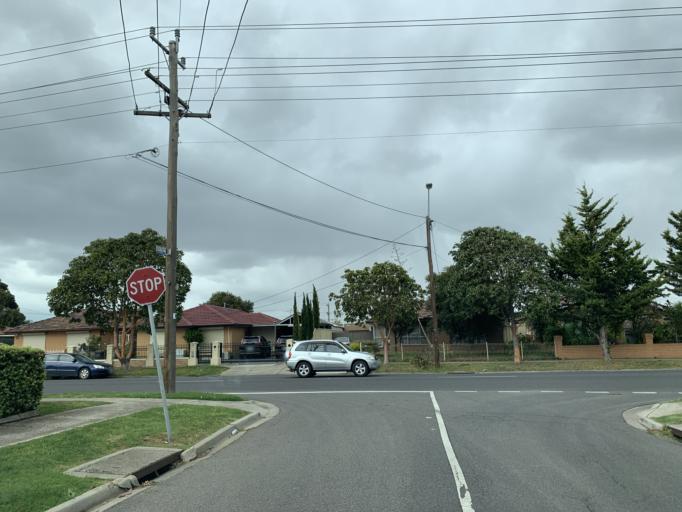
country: AU
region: Victoria
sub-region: Brimbank
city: Kealba
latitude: -37.7469
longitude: 144.8237
